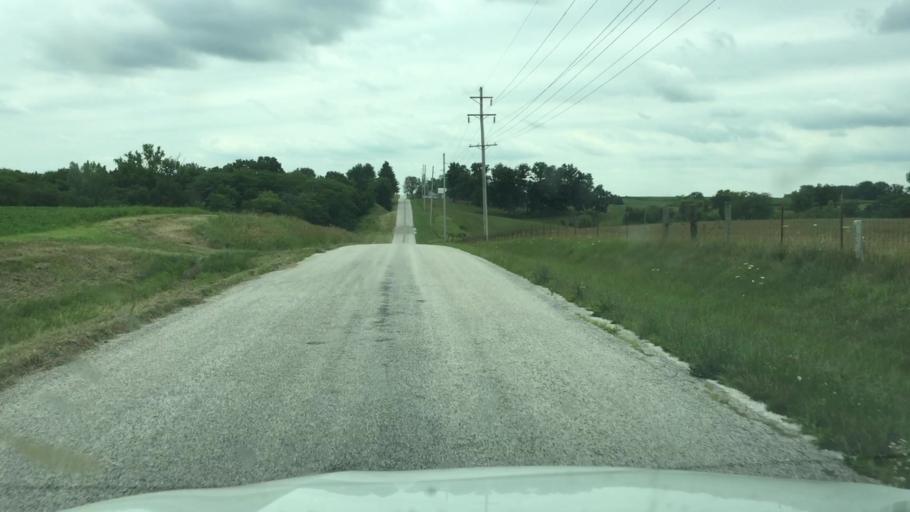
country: US
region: Illinois
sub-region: Hancock County
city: Carthage
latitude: 40.3286
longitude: -91.0826
